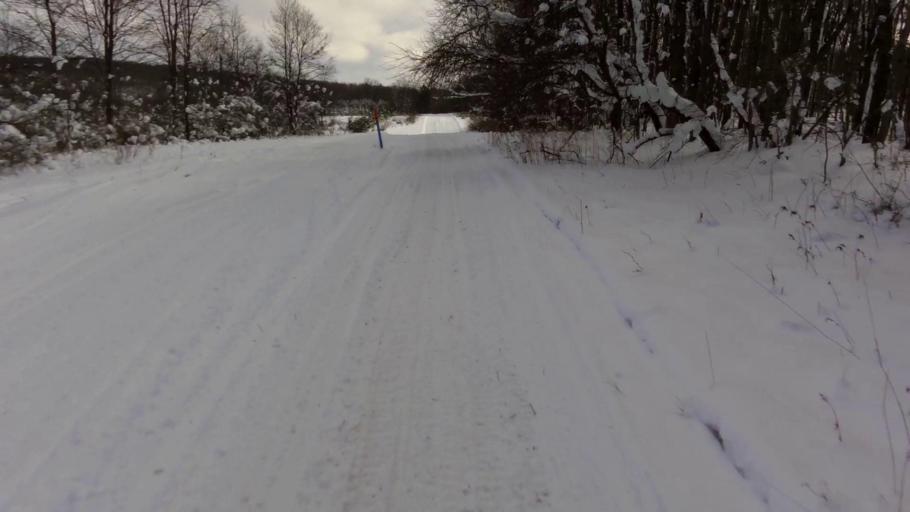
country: US
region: New York
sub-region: Cattaraugus County
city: Franklinville
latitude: 42.3125
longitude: -78.5349
